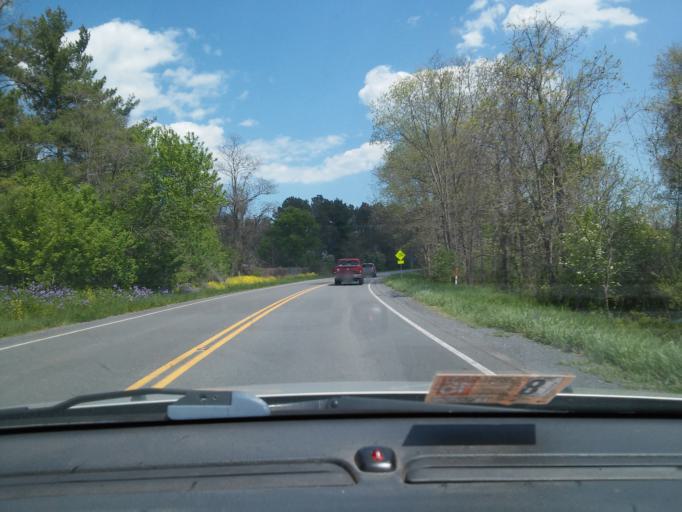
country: US
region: Virginia
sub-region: Warren County
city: Front Royal
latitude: 38.8790
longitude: -78.1533
